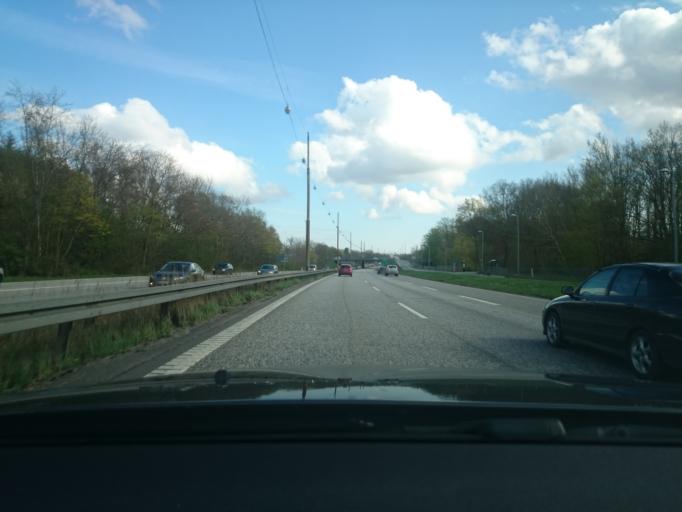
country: DK
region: Capital Region
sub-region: Herlev Kommune
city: Herlev
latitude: 55.7602
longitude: 12.4412
